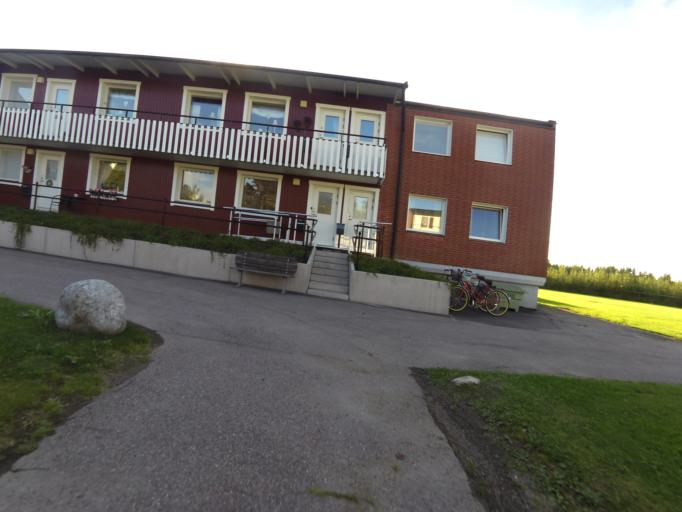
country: SE
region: Gaevleborg
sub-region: Gavle Kommun
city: Gavle
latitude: 60.7283
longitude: 17.1700
